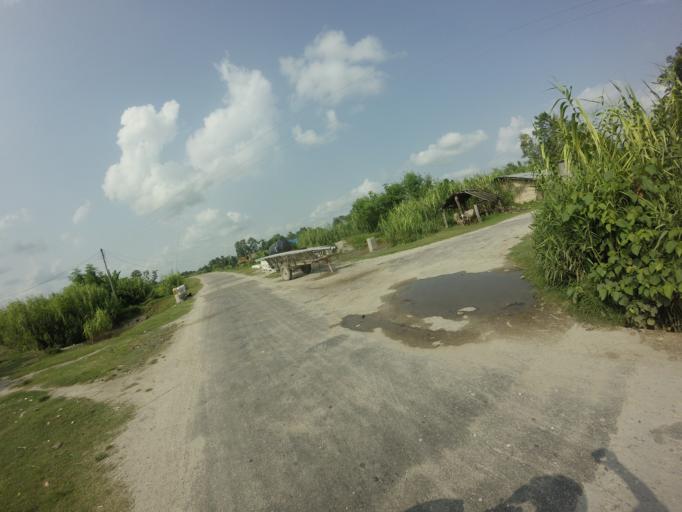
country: NP
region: Far Western
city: Tikapur
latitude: 28.4675
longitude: 81.0751
